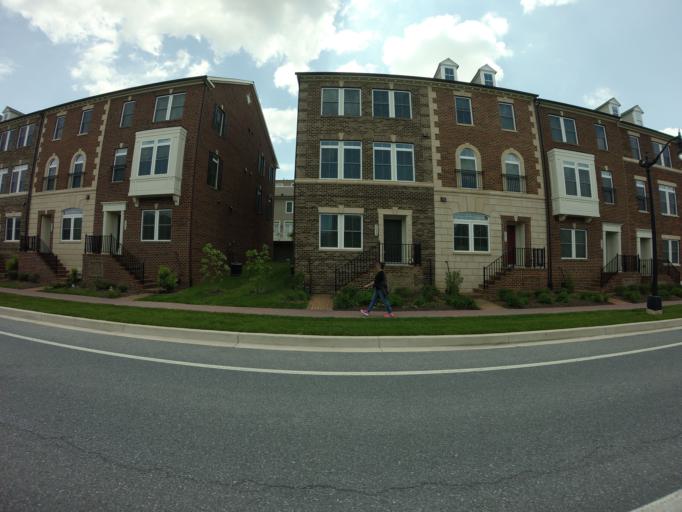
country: US
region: Maryland
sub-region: Frederick County
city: Urbana
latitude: 39.3308
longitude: -77.3581
